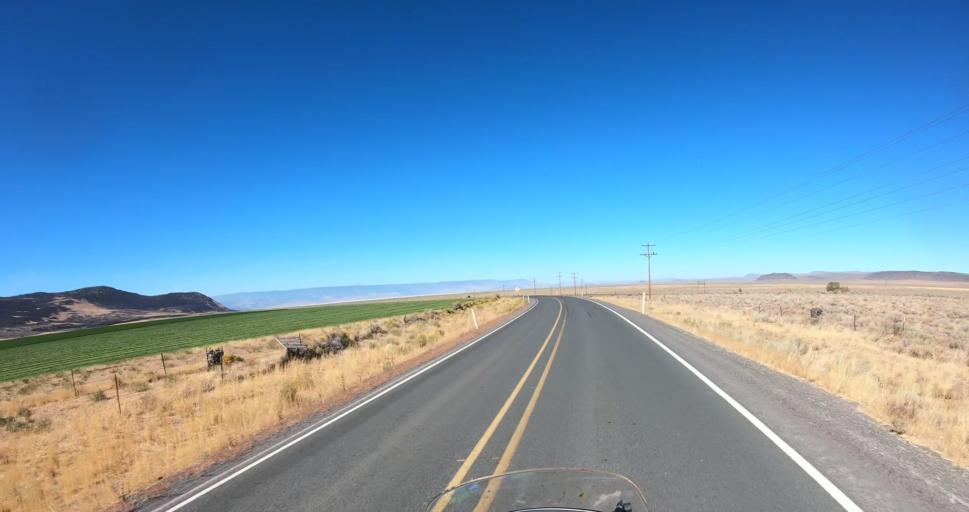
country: US
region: Oregon
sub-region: Lake County
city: Lakeview
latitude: 42.7029
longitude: -120.5476
